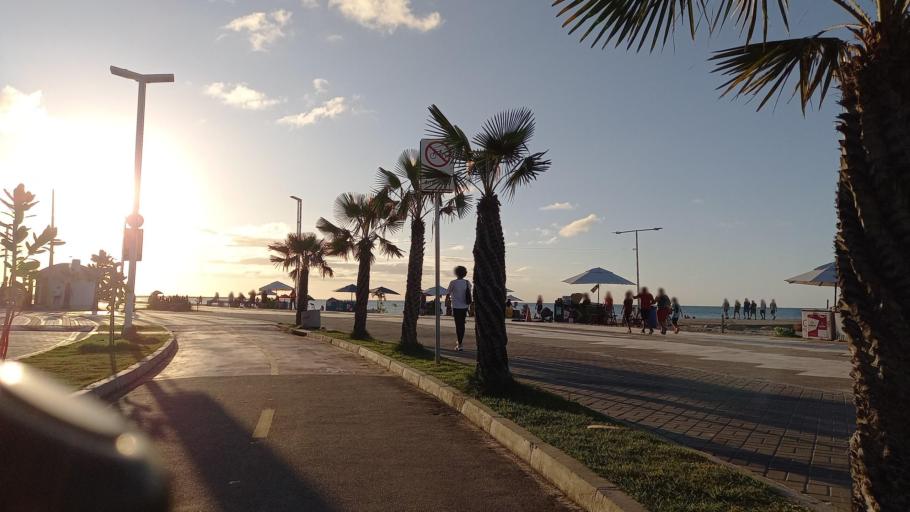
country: BR
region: Ceara
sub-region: Fortaleza
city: Fortaleza
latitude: -3.7250
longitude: -38.4944
